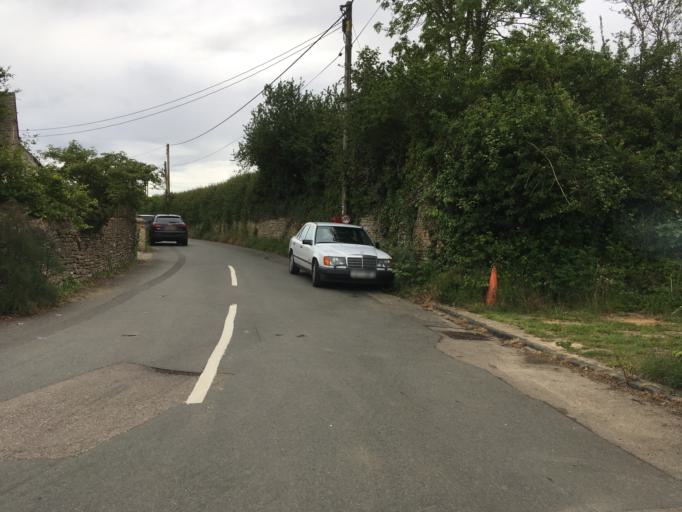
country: GB
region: England
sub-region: Wiltshire
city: Norton
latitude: 51.5805
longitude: -2.1954
